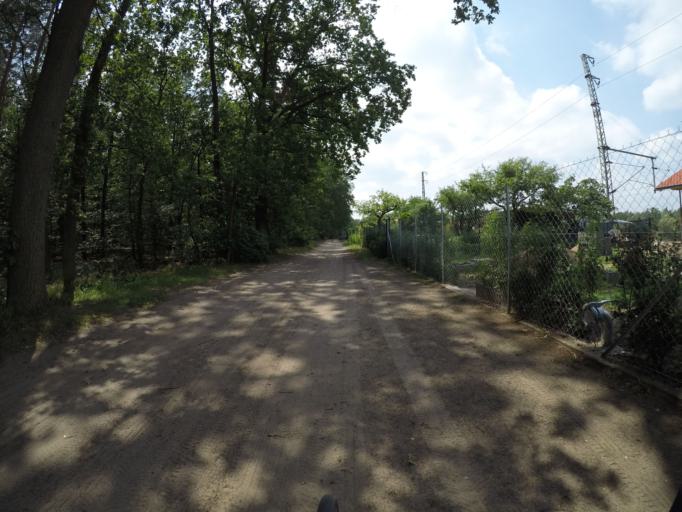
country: DE
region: Berlin
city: Grunewald
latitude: 52.4790
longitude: 13.2521
